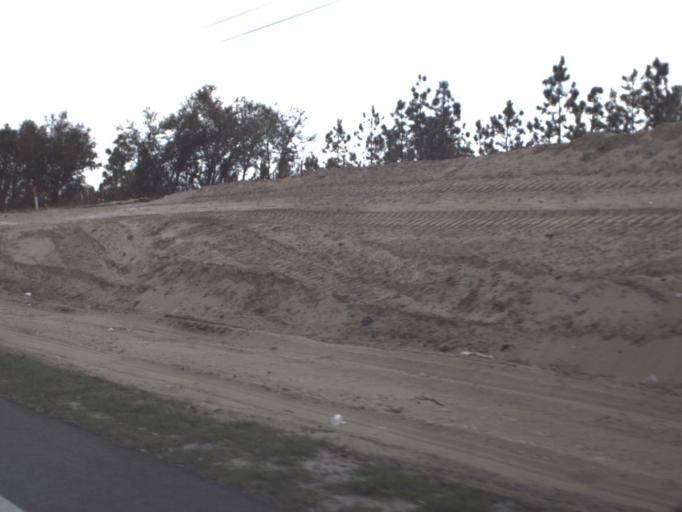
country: US
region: Florida
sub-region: Lake County
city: Clermont
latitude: 28.4401
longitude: -81.7170
